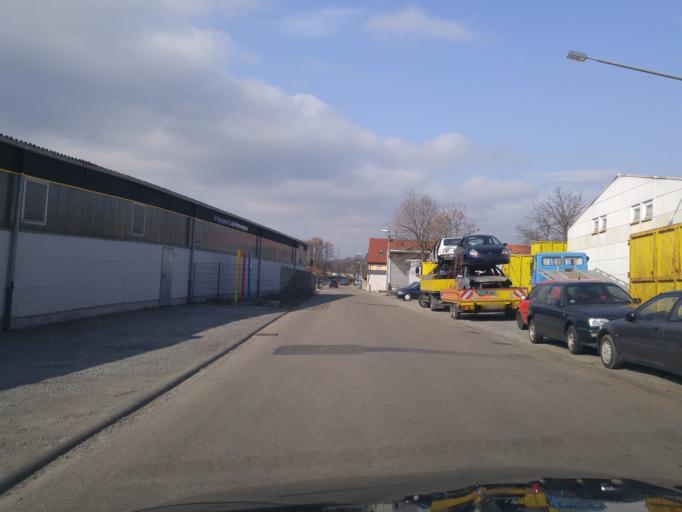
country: DE
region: Baden-Wuerttemberg
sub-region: Regierungsbezirk Stuttgart
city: Abstatt
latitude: 49.0564
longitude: 9.2806
